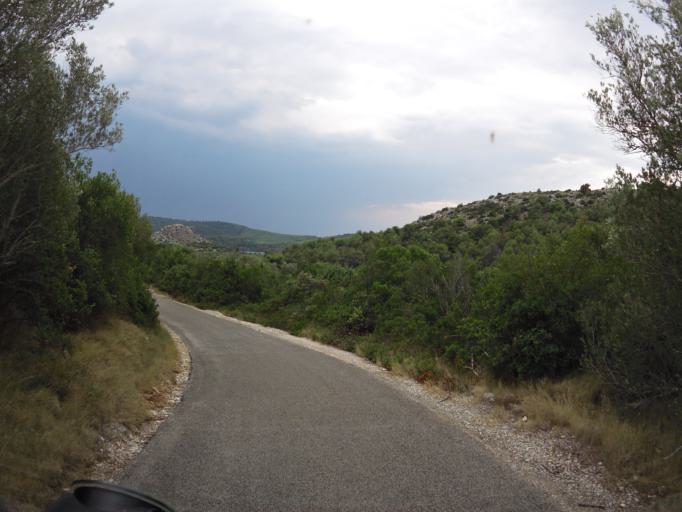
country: HR
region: Zadarska
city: Sali
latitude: 43.9312
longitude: 15.1384
